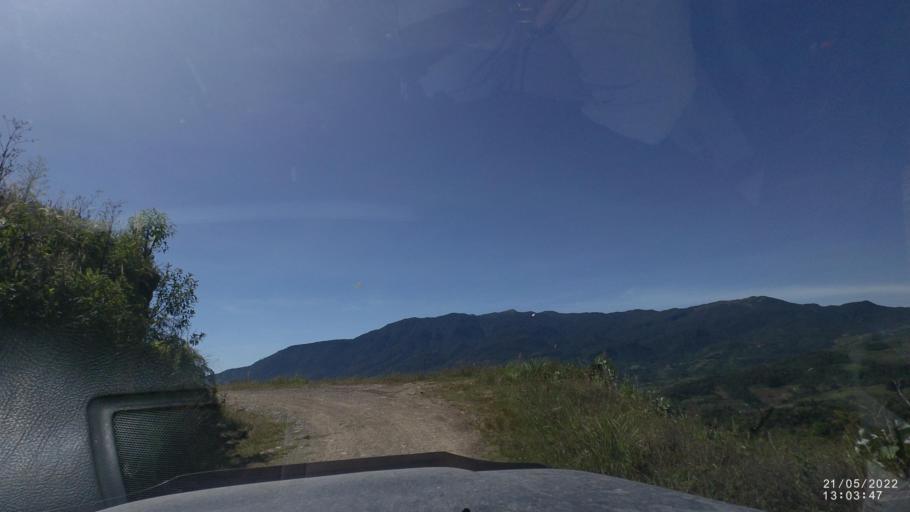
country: BO
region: Cochabamba
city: Colomi
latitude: -17.1580
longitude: -65.9519
